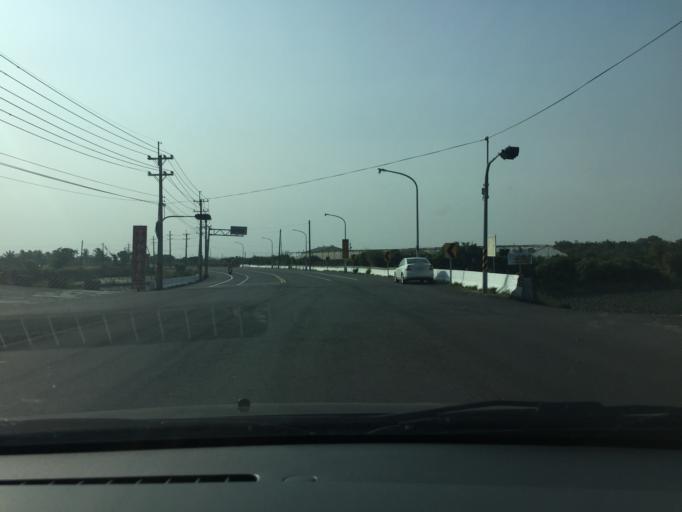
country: TW
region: Taiwan
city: Xinying
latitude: 23.1996
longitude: 120.2941
